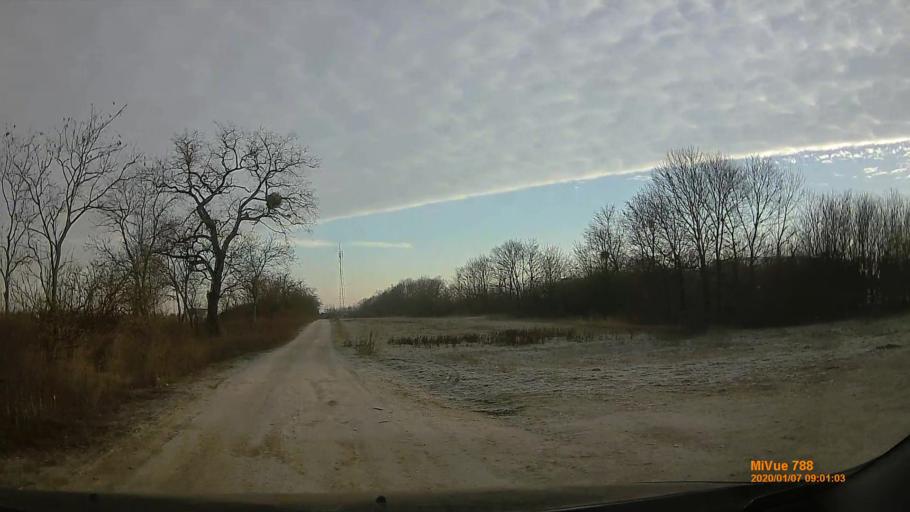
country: HU
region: Gyor-Moson-Sopron
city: Rajka
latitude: 47.9891
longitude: 17.1881
